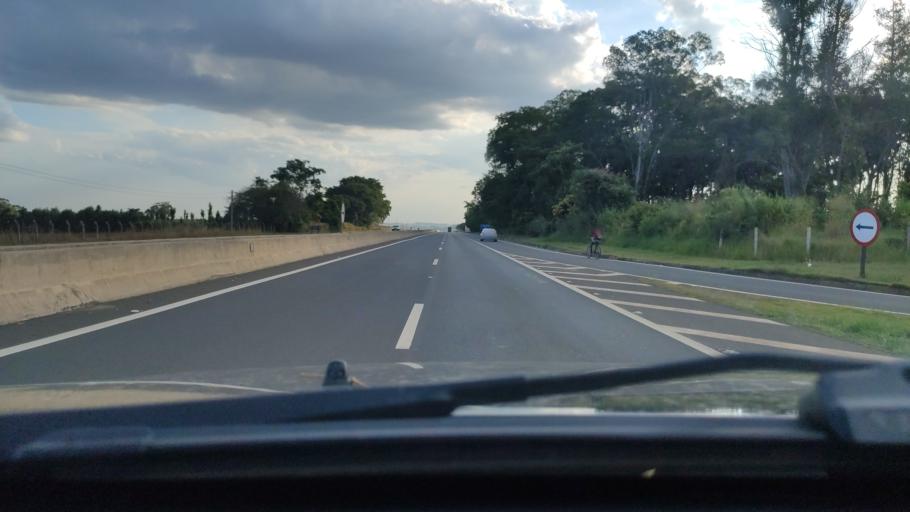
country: BR
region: Sao Paulo
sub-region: Artur Nogueira
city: Artur Nogueira
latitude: -22.4685
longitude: -47.1129
